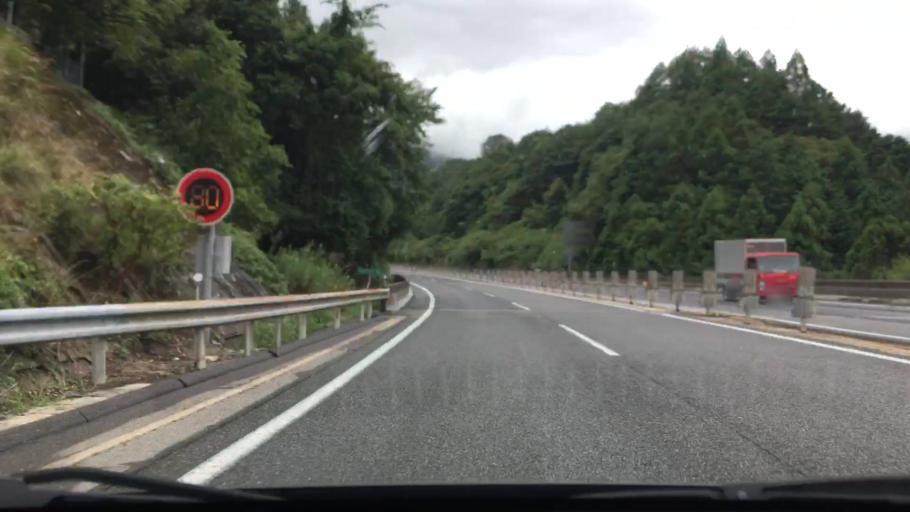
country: JP
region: Hiroshima
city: Hiroshima-shi
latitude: 34.5581
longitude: 132.4503
